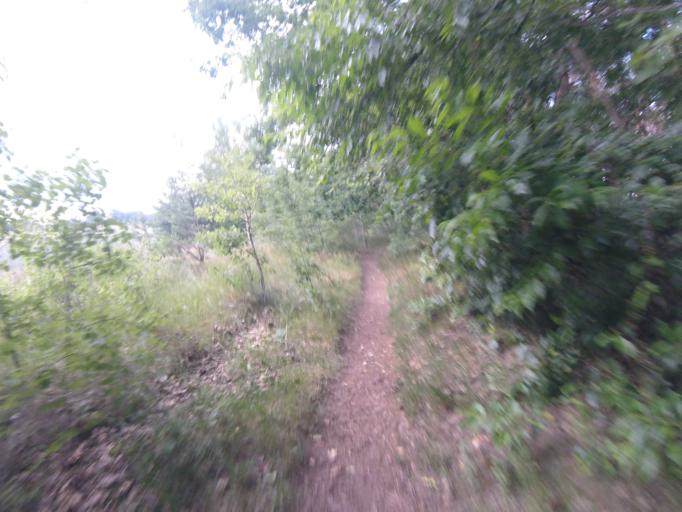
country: DE
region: Brandenburg
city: Bestensee
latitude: 52.2516
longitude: 13.6238
